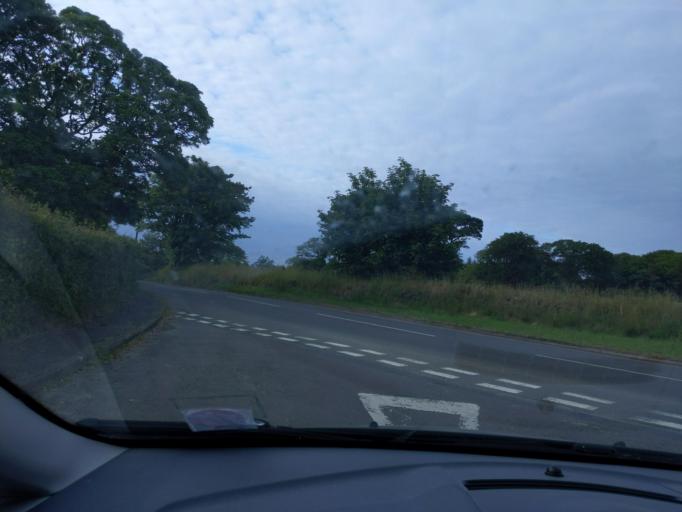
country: IM
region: Ramsey
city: Ramsey
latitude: 54.3643
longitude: -4.4375
